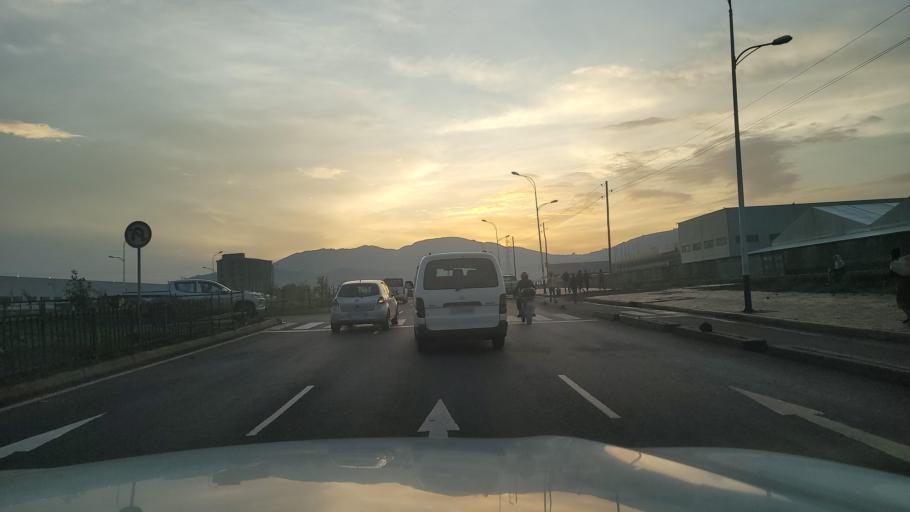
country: ET
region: Adis Abeba
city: Addis Ababa
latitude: 8.9500
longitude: 38.7057
